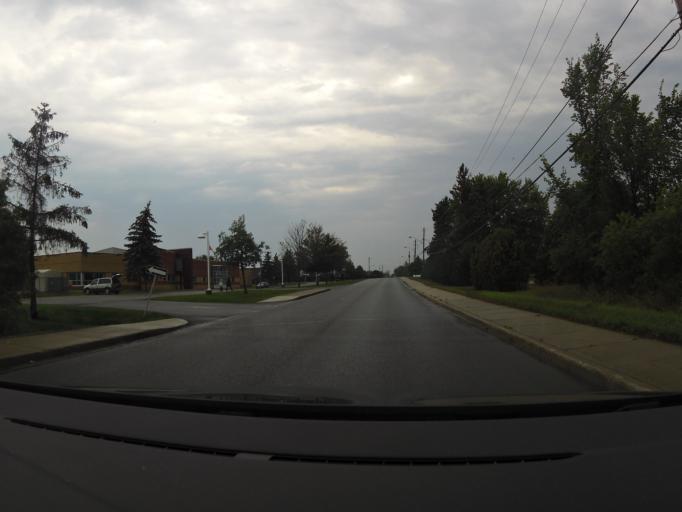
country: CA
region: Ontario
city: Carleton Place
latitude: 45.2307
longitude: -76.1828
